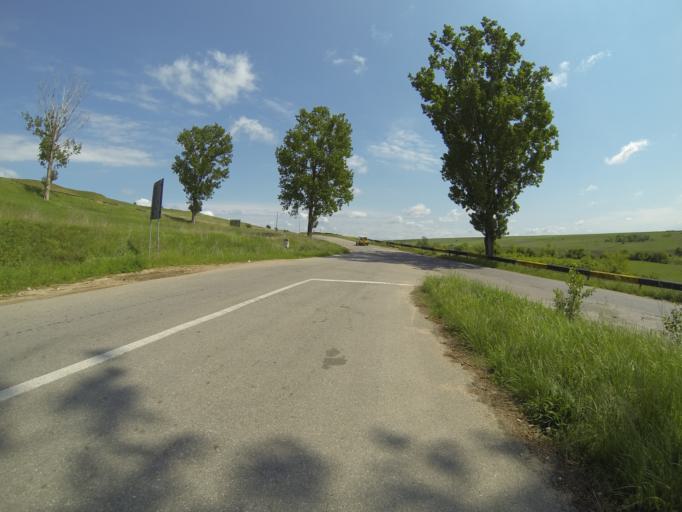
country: RO
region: Dolj
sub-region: Comuna Salcuta
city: Salcuta
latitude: 44.2588
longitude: 23.4551
